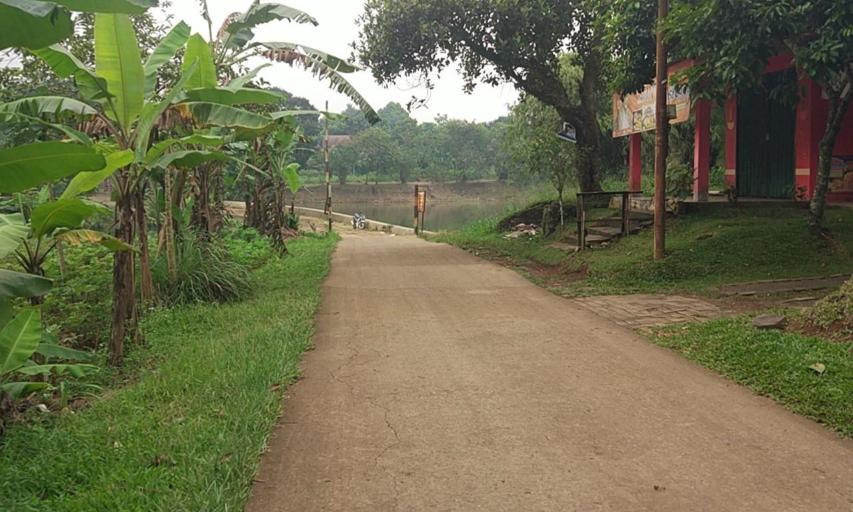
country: ID
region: West Java
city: Ciampea
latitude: -6.5130
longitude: 106.7697
